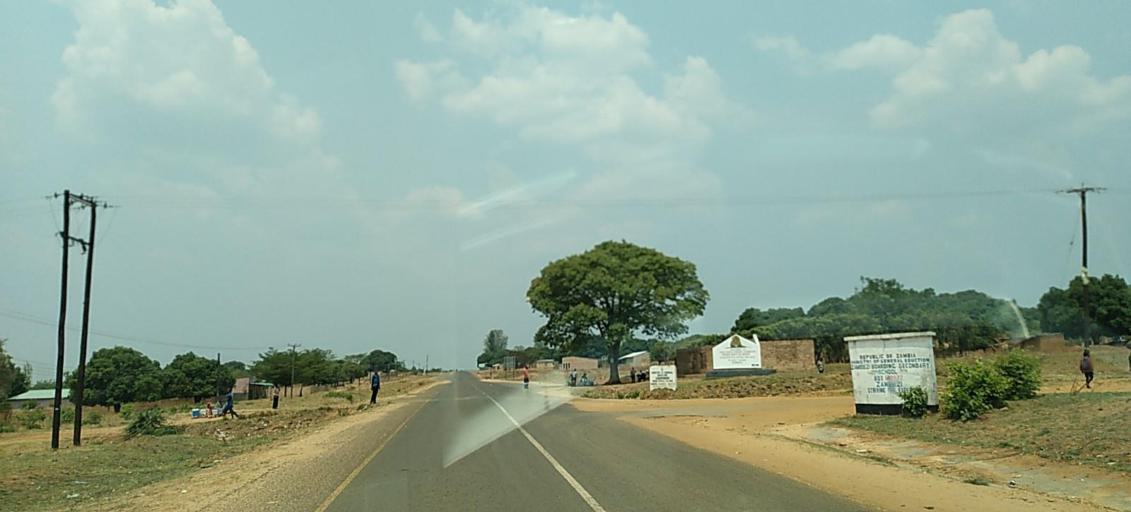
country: ZM
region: North-Western
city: Zambezi
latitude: -13.5507
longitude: 23.1117
